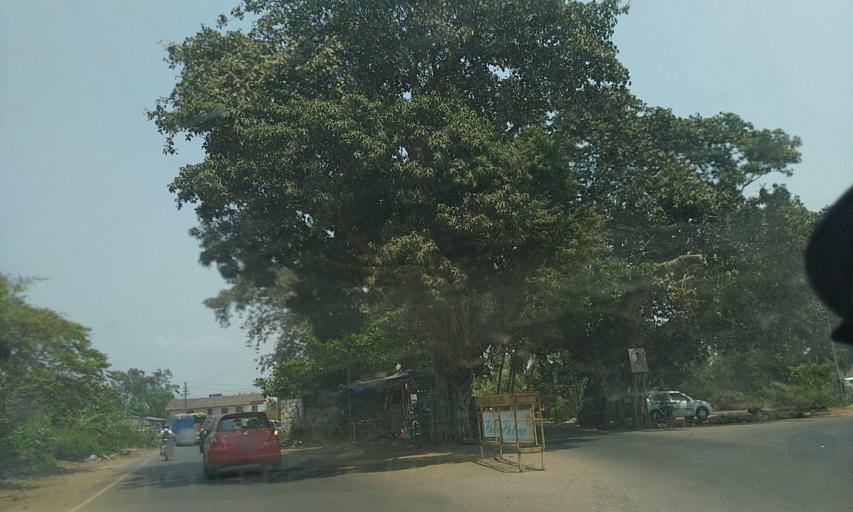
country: IN
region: Goa
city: Calangute
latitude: 15.5476
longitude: 73.7713
